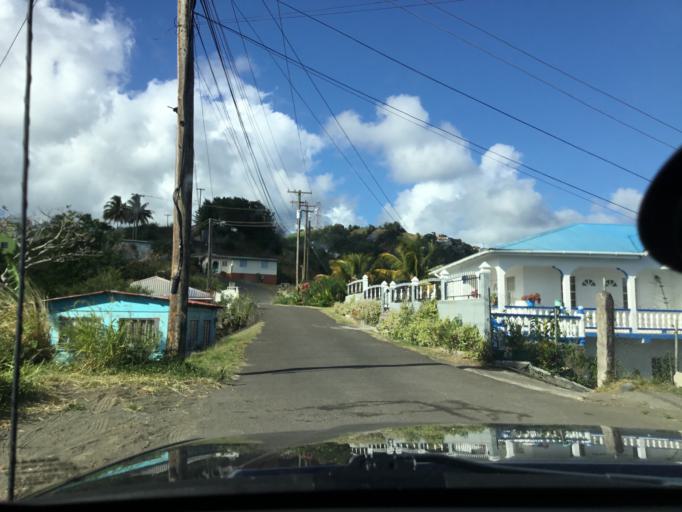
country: VC
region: Saint George
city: Kingstown
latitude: 13.1553
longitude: -61.1776
